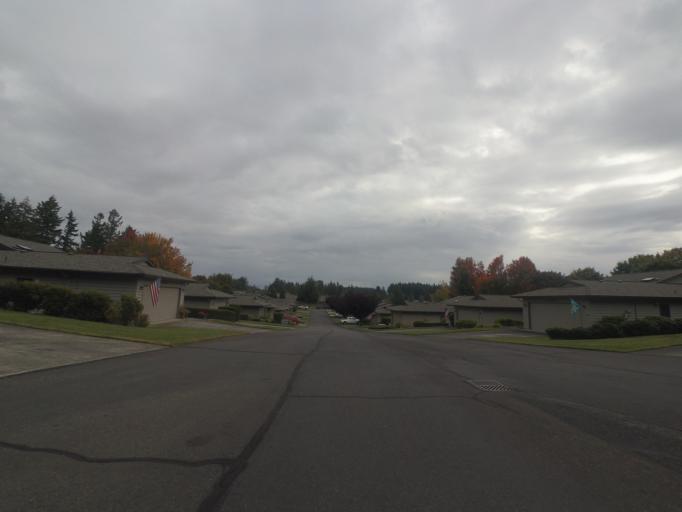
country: US
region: Washington
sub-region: Pierce County
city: University Place
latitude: 47.2090
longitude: -122.5447
